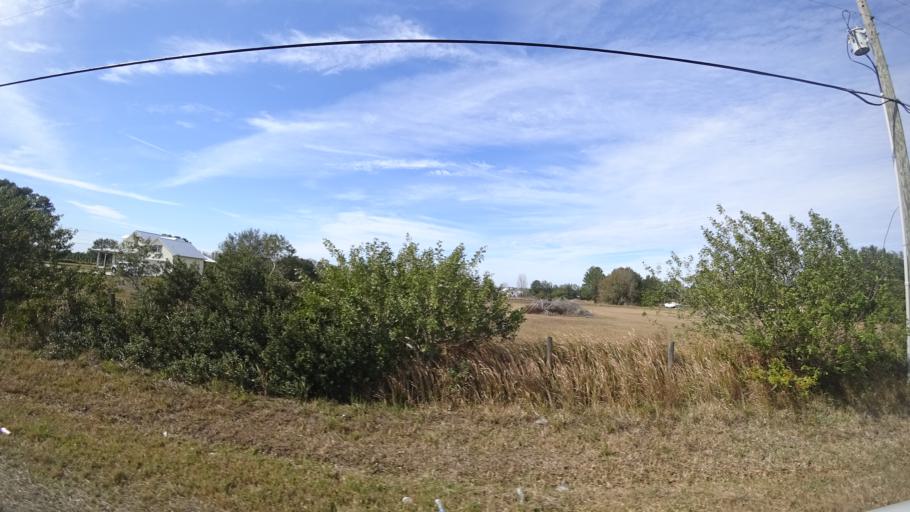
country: US
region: Florida
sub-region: Manatee County
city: Ellenton
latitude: 27.5527
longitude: -82.3690
